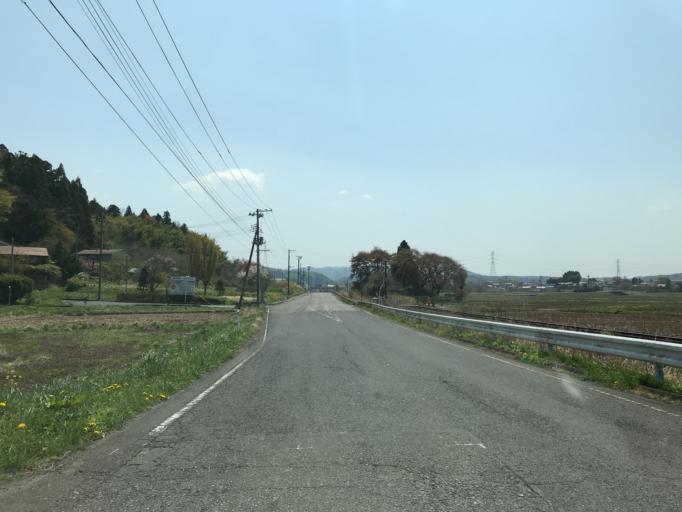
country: JP
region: Fukushima
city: Ishikawa
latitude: 37.0919
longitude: 140.4115
